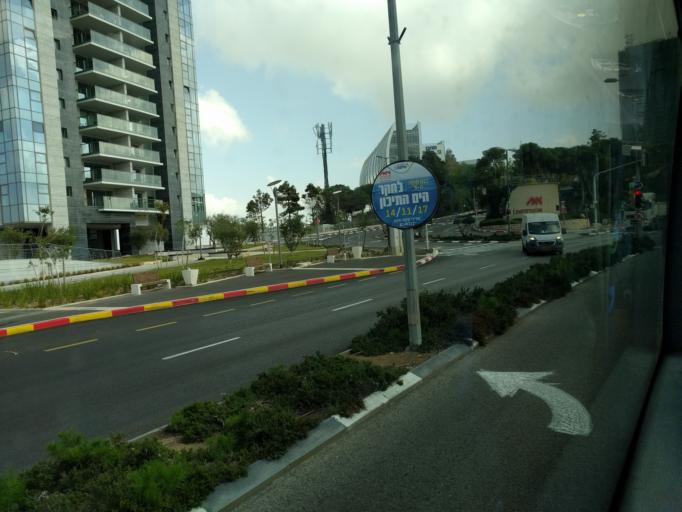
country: IL
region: Haifa
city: Nesher
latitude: 32.7654
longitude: 35.0138
